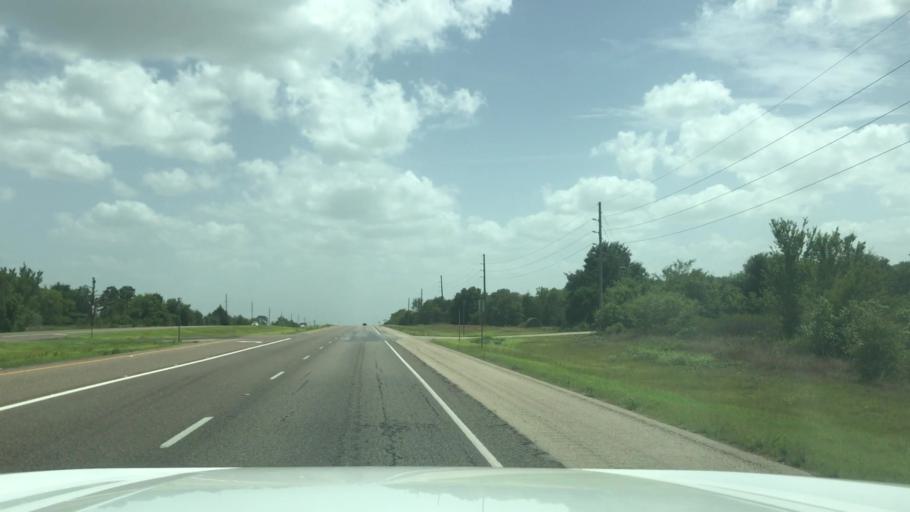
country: US
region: Texas
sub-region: Robertson County
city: Calvert
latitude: 31.0848
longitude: -96.7140
